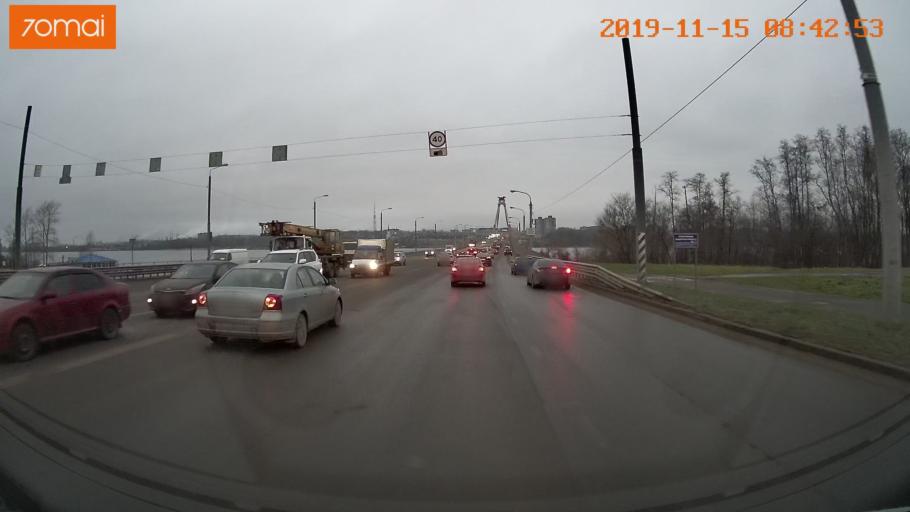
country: RU
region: Vologda
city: Cherepovets
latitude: 59.1064
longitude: 37.9057
